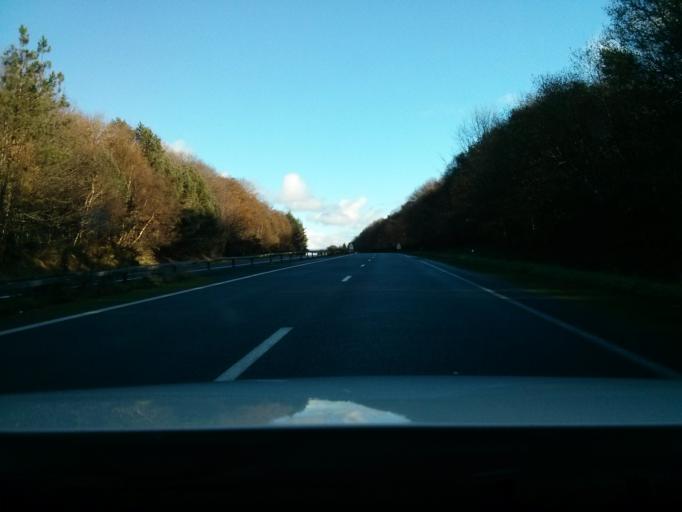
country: FR
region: Brittany
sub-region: Departement du Finistere
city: Plouigneau
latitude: 48.5731
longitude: -3.6855
